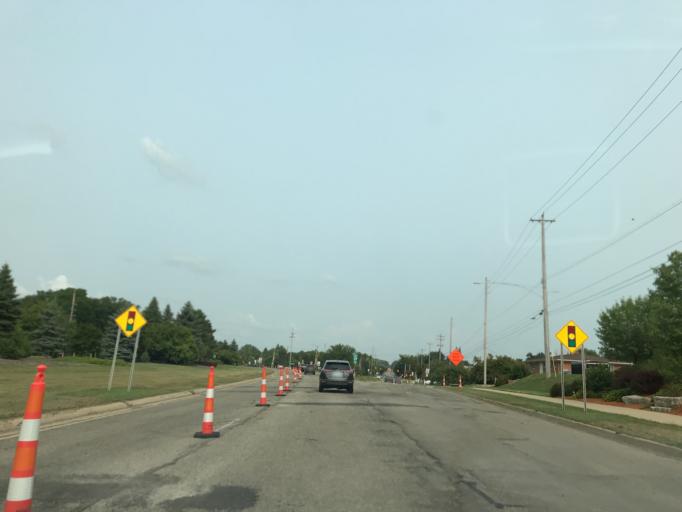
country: US
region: Michigan
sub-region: Ingham County
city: East Lansing
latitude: 42.7469
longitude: -84.4665
